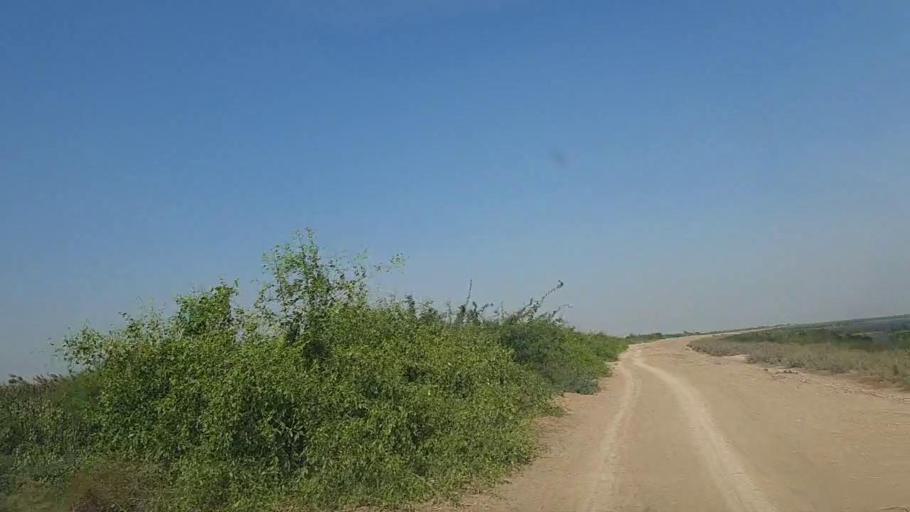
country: PK
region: Sindh
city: Daro Mehar
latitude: 24.9209
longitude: 68.0784
